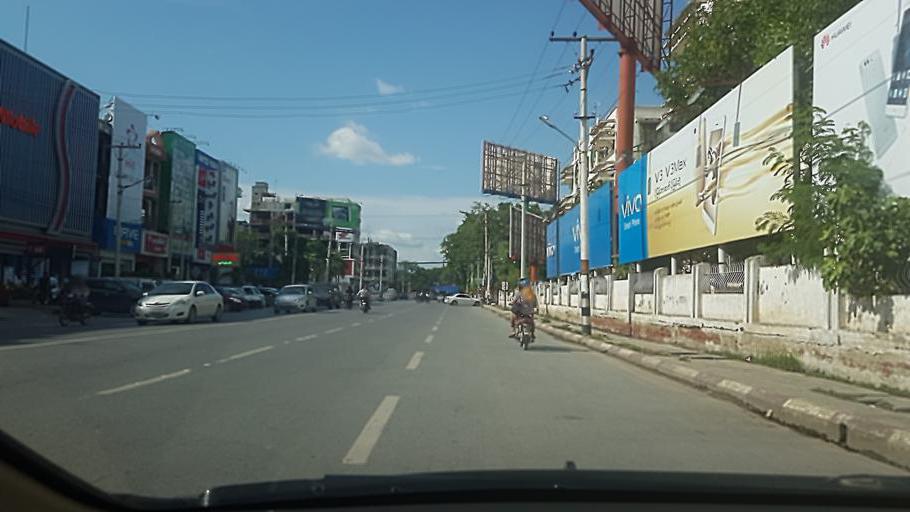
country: MM
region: Mandalay
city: Mandalay
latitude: 21.9806
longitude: 96.0872
